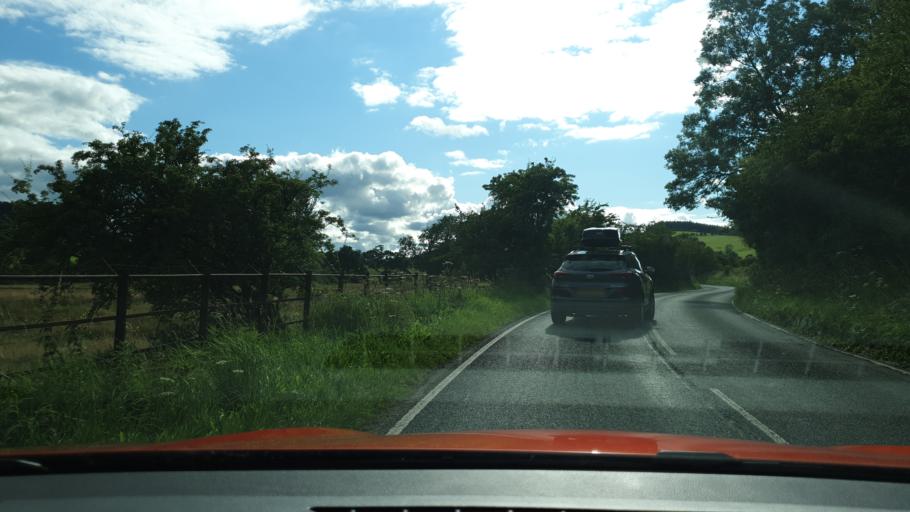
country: GB
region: England
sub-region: Cumbria
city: Penrith
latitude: 54.6237
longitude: -2.8162
